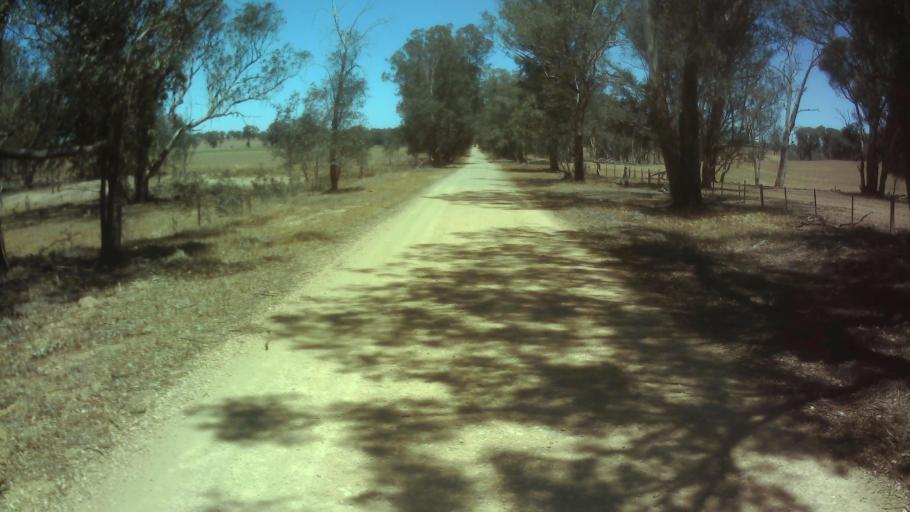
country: AU
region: New South Wales
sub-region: Weddin
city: Grenfell
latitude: -33.9140
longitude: 148.2136
